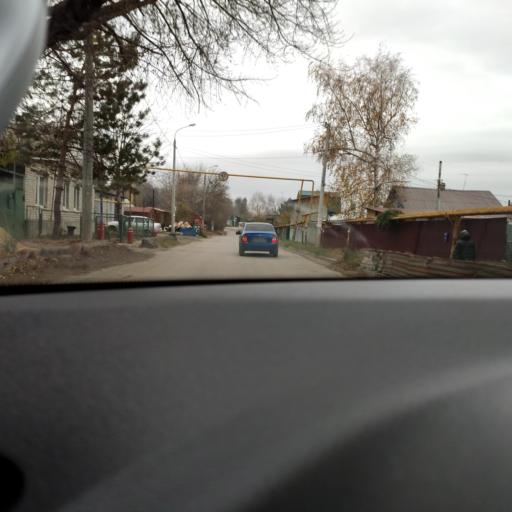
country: RU
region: Samara
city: Samara
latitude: 53.1771
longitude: 50.1484
